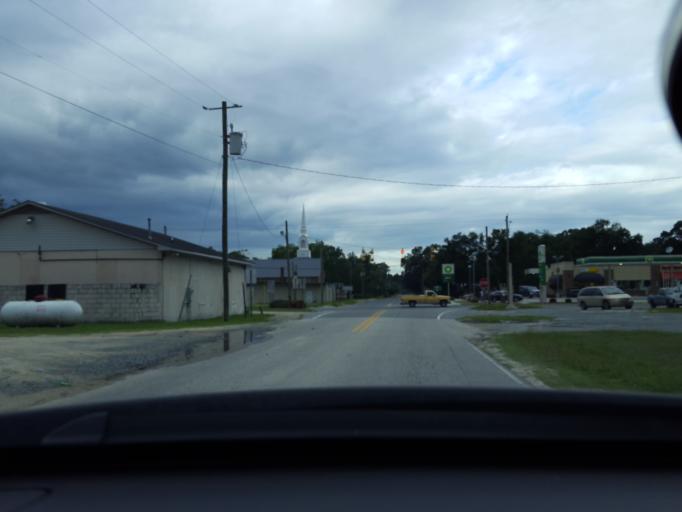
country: US
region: North Carolina
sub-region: Sampson County
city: Roseboro
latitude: 34.7853
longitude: -78.3935
